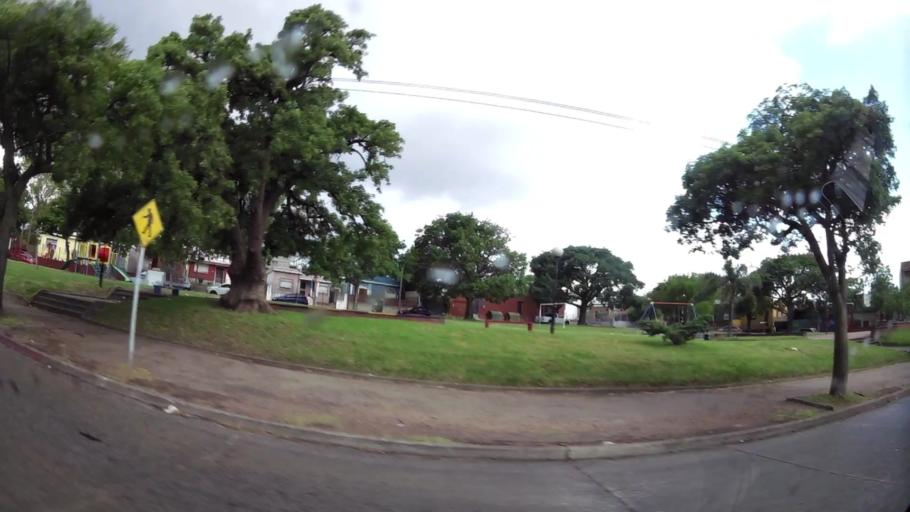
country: UY
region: Montevideo
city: Montevideo
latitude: -34.8561
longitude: -56.1743
